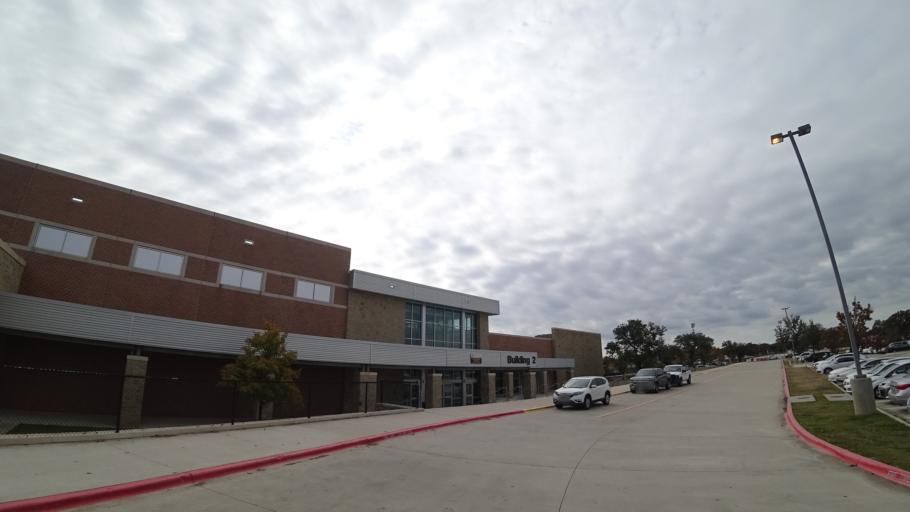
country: US
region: Texas
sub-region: Williamson County
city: Anderson Mill
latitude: 30.3987
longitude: -97.8252
